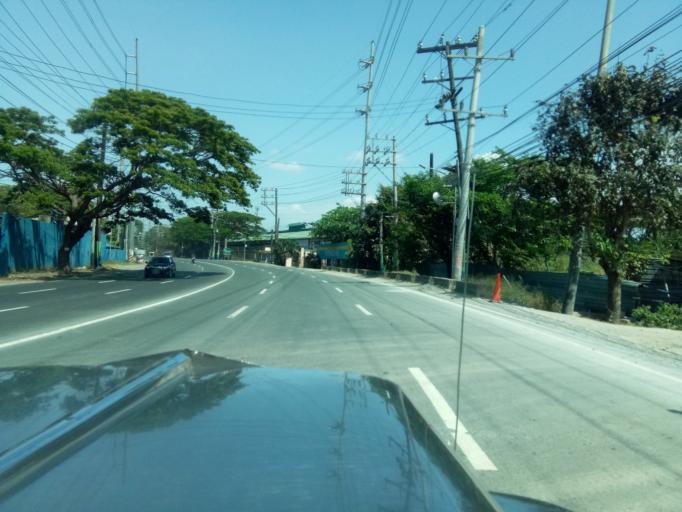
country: PH
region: Calabarzon
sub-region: Province of Cavite
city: Manggahan
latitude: 14.2914
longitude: 120.9260
